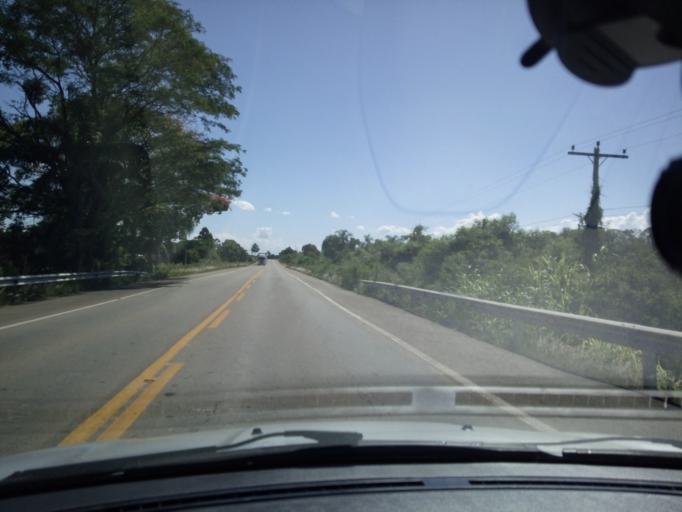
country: BR
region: Rio Grande do Sul
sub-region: Santa Maria
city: Santa Maria
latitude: -29.7324
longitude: -53.5183
